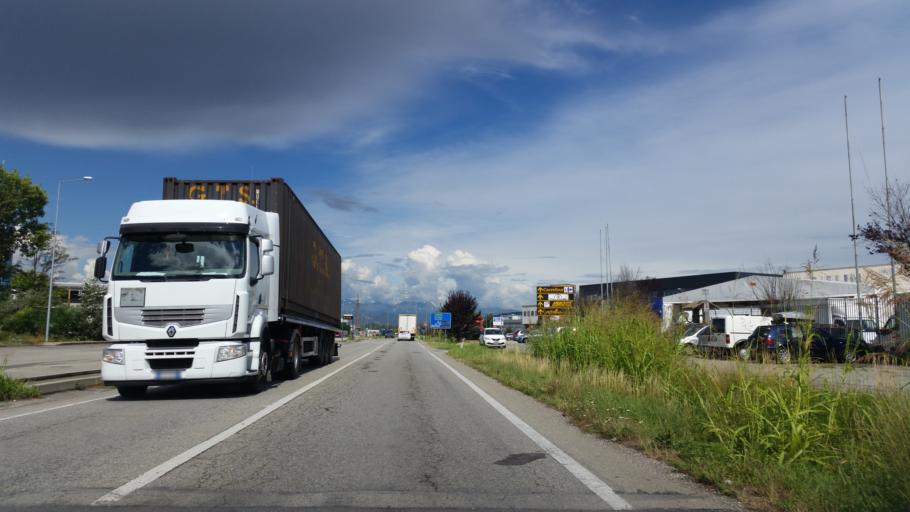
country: IT
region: Piedmont
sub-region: Provincia di Torino
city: Santena
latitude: 44.9534
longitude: 7.7944
